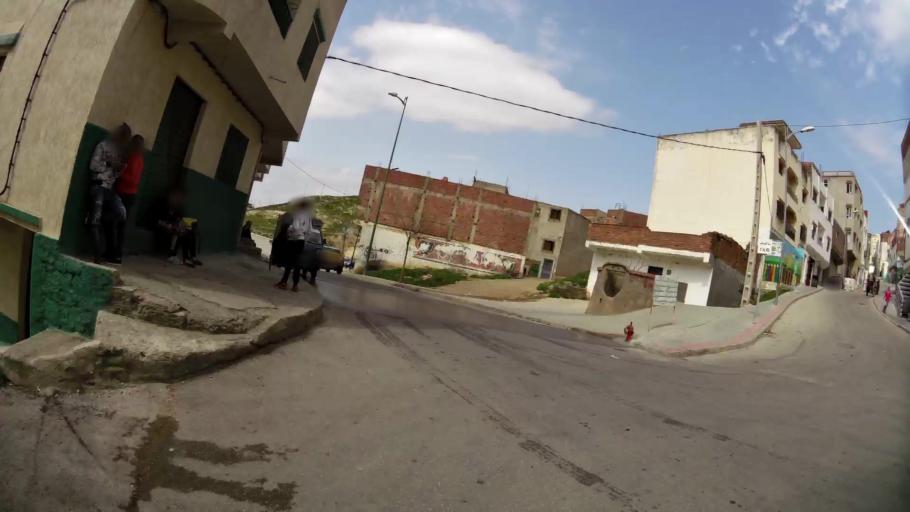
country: MA
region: Tanger-Tetouan
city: Tetouan
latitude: 35.5801
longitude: -5.3901
